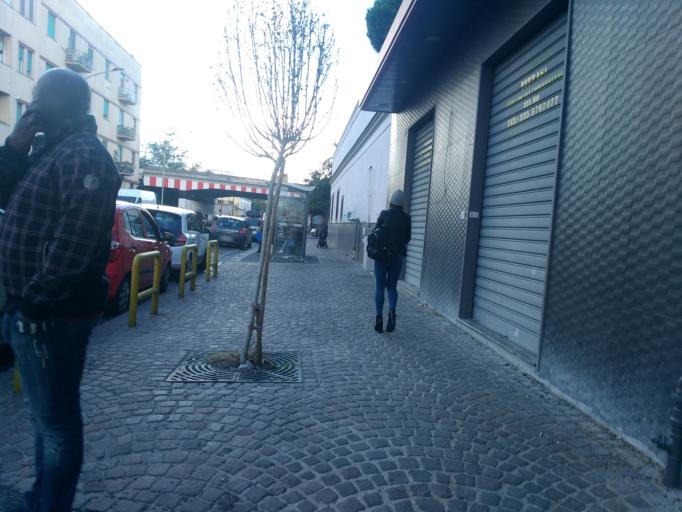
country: IT
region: Campania
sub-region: Provincia di Napoli
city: Napoli
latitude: 40.8497
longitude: 14.2847
